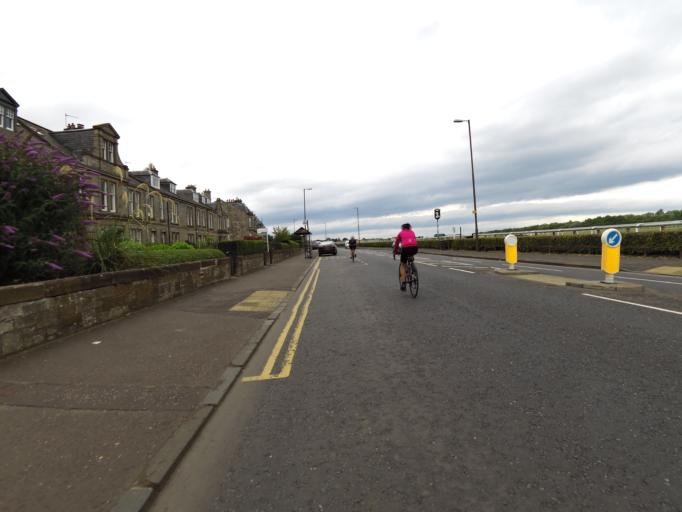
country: GB
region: Scotland
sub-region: East Lothian
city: Musselburgh
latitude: 55.9454
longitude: -3.0344
